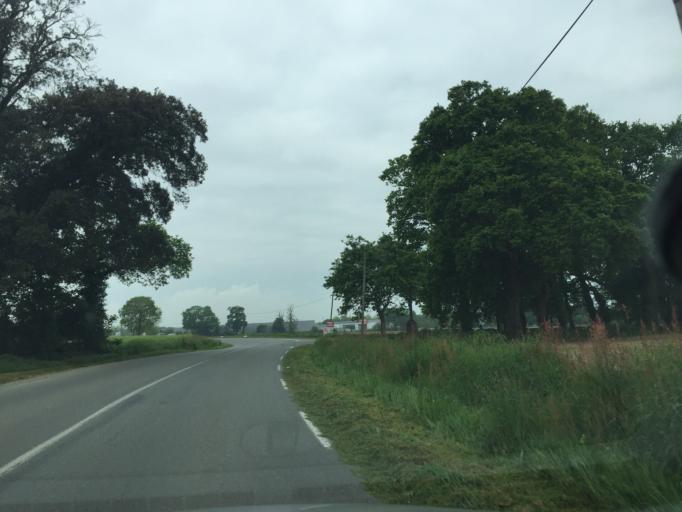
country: FR
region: Brittany
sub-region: Departement des Cotes-d'Armor
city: Matignon
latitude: 48.5966
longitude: -2.2803
